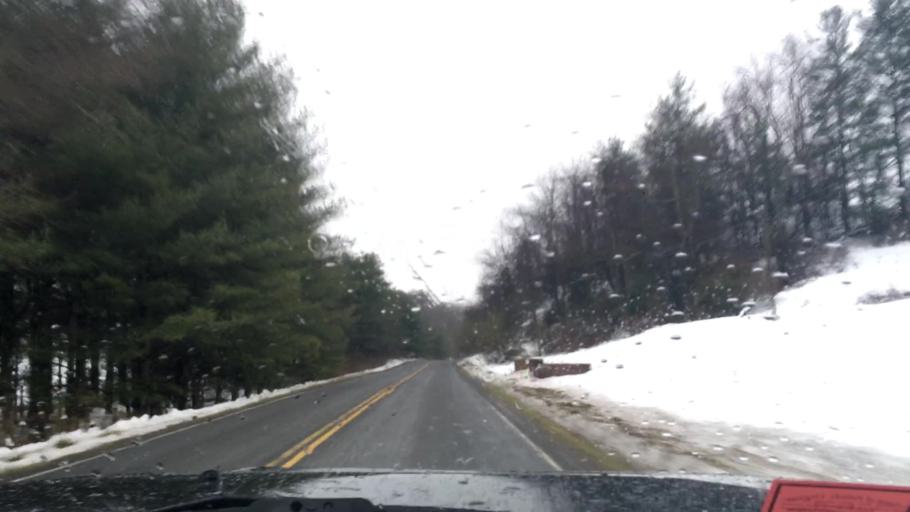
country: US
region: Virginia
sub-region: Pulaski County
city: Pulaski
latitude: 37.0220
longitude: -80.7110
